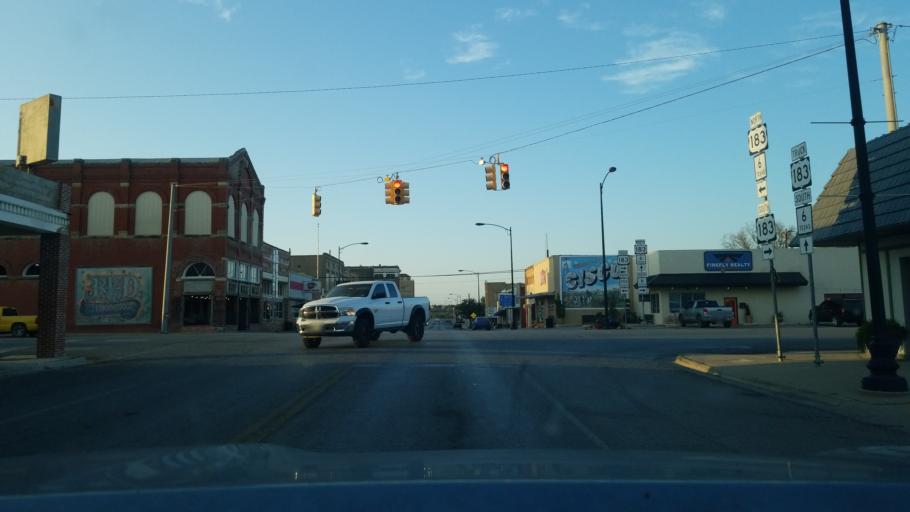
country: US
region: Texas
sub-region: Eastland County
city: Cisco
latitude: 32.3879
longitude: -98.9792
